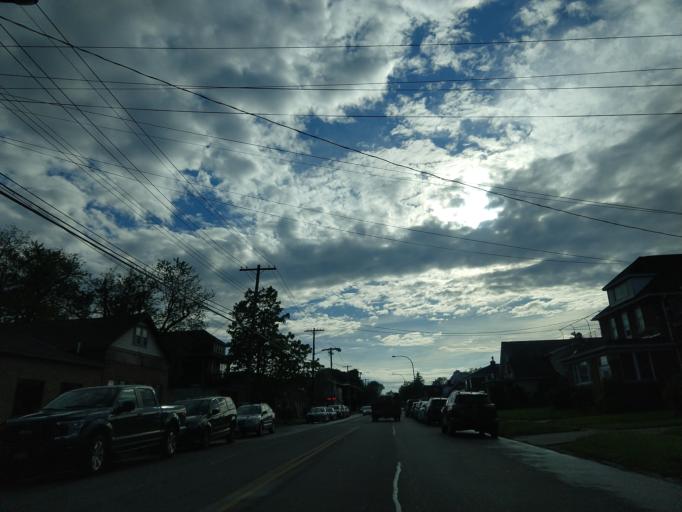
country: US
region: New York
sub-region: Erie County
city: Lackawanna
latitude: 42.8283
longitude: -78.8064
